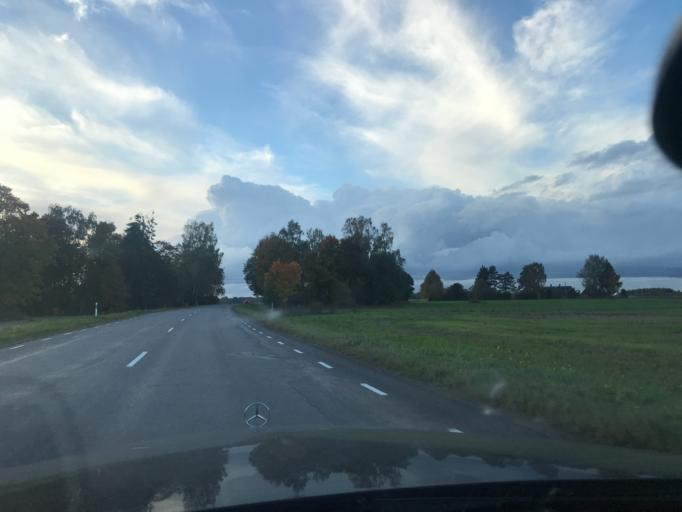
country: EE
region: Vorumaa
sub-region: Antsla vald
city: Vana-Antsla
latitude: 57.8959
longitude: 26.4879
